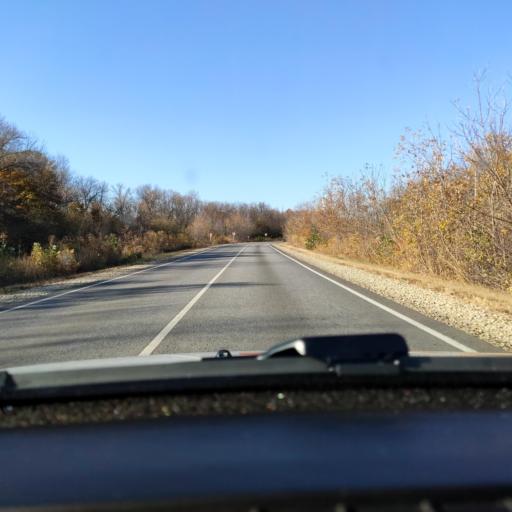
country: RU
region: Voronezj
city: Zemlyansk
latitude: 51.8496
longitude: 38.7979
